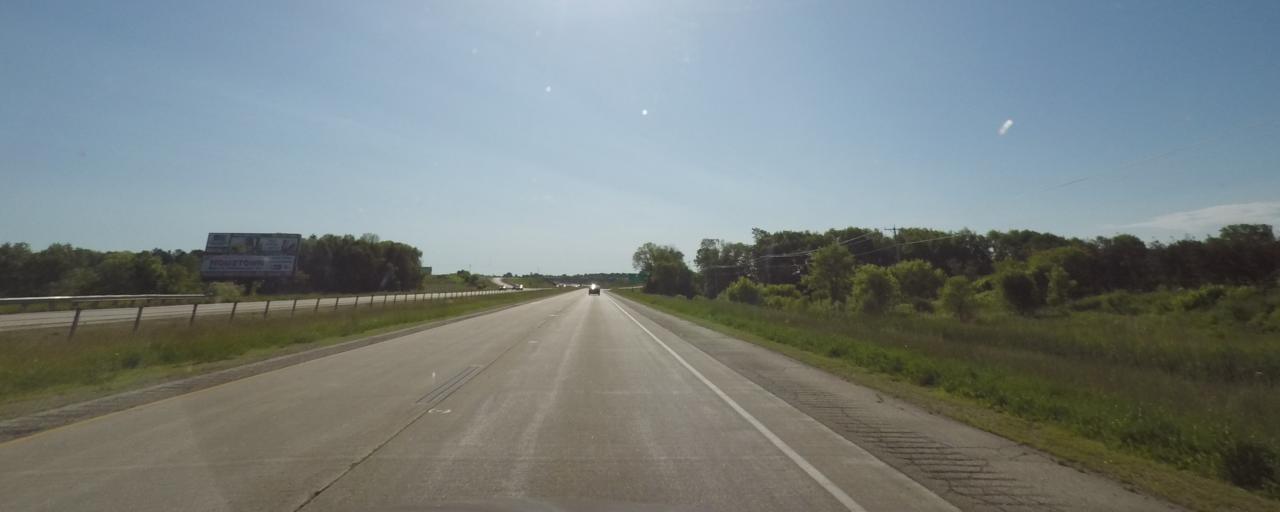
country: US
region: Wisconsin
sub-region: Dodge County
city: Beaver Dam
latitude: 43.4357
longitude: -88.8524
